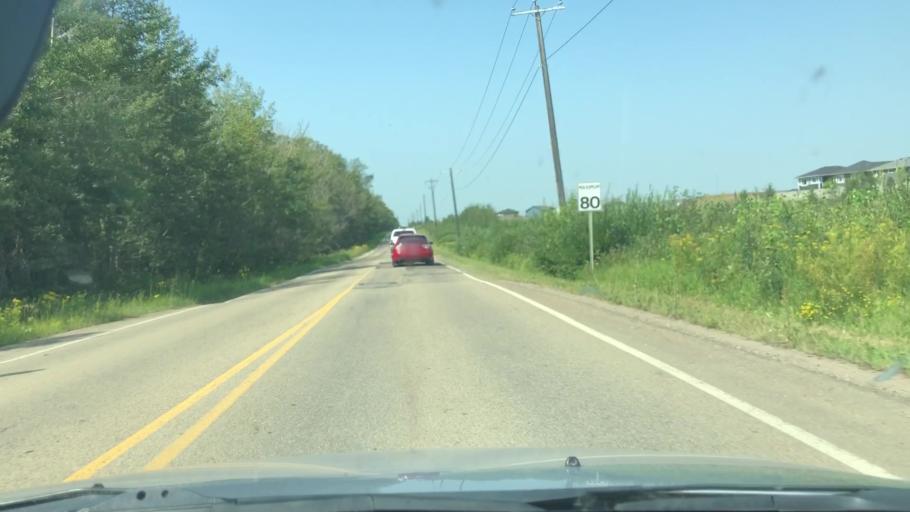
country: CA
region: Alberta
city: St. Albert
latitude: 53.5122
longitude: -113.6921
